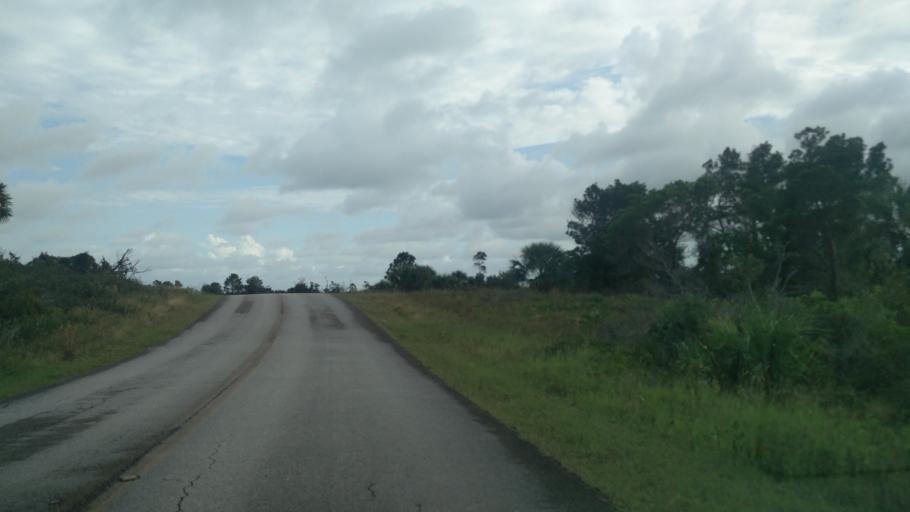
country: US
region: Florida
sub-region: Palm Beach County
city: Tequesta
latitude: 27.0108
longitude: -80.1096
